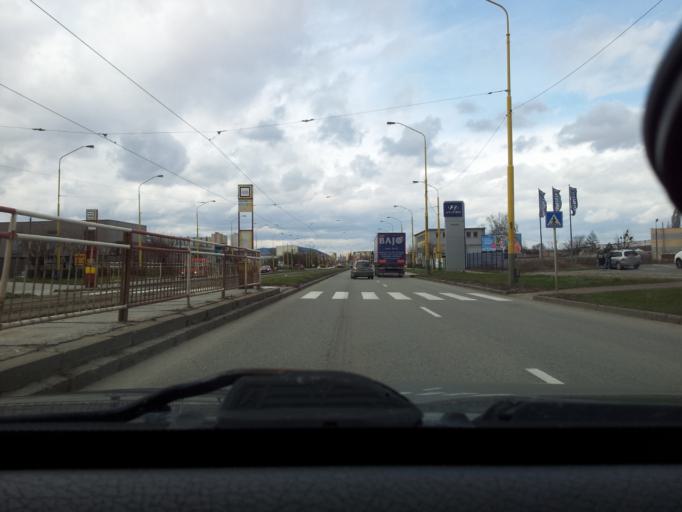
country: SK
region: Kosicky
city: Kosice
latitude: 48.6921
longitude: 21.2654
